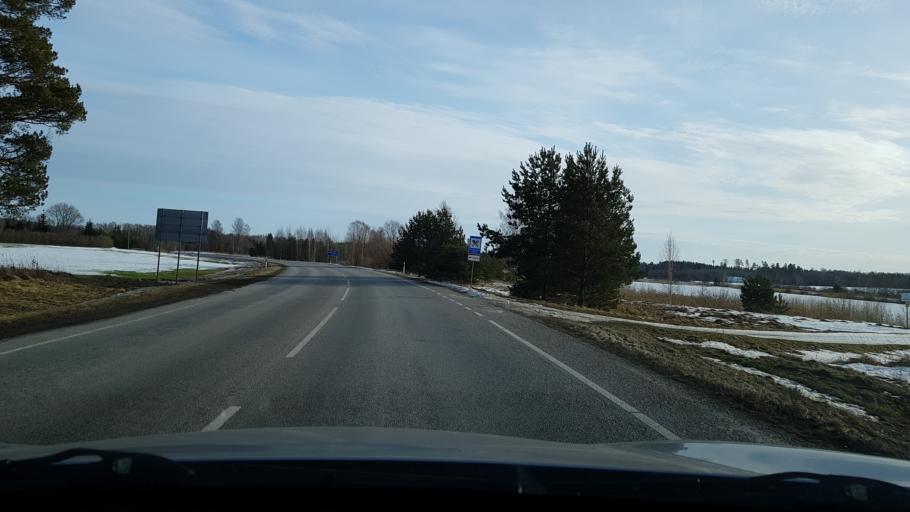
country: EE
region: Viljandimaa
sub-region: Viljandi linn
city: Viljandi
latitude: 58.3406
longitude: 25.4692
